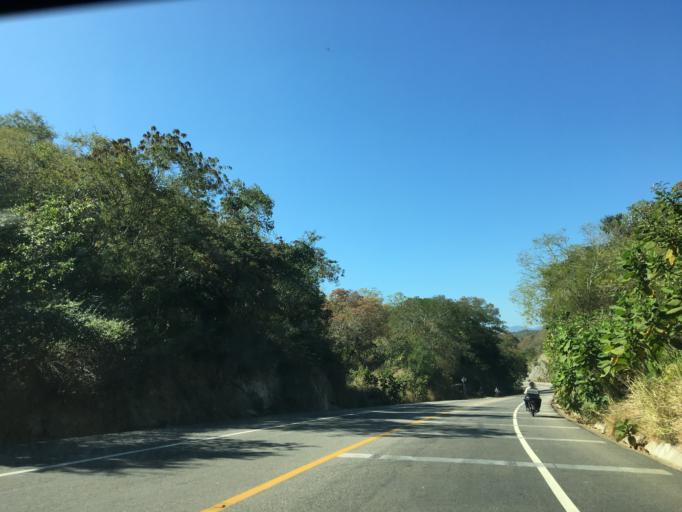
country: MX
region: Oaxaca
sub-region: Santa Maria Huatulco
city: Sector H Tres
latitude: 15.7731
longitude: -96.2308
